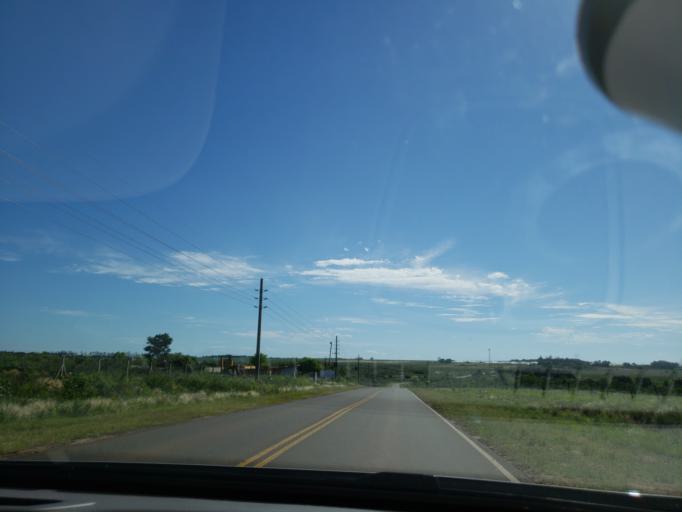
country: AR
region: Misiones
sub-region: Departamento de Capital
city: Posadas
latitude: -27.3883
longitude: -55.9795
